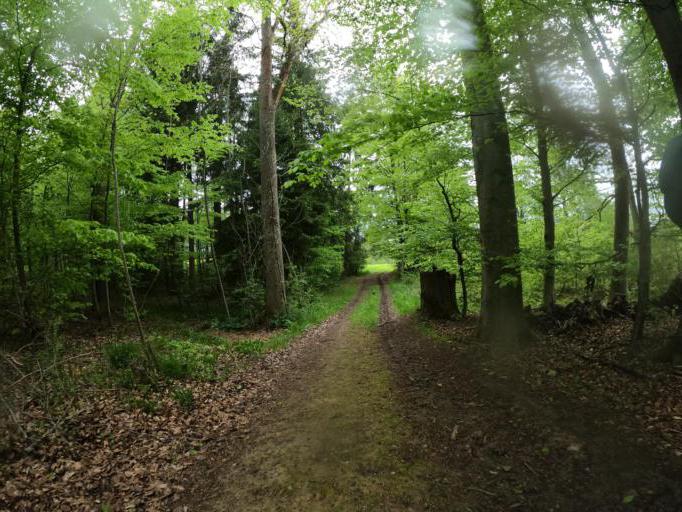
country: DE
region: Baden-Wuerttemberg
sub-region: Regierungsbezirk Stuttgart
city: Herrenberg
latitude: 48.5755
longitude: 8.8296
